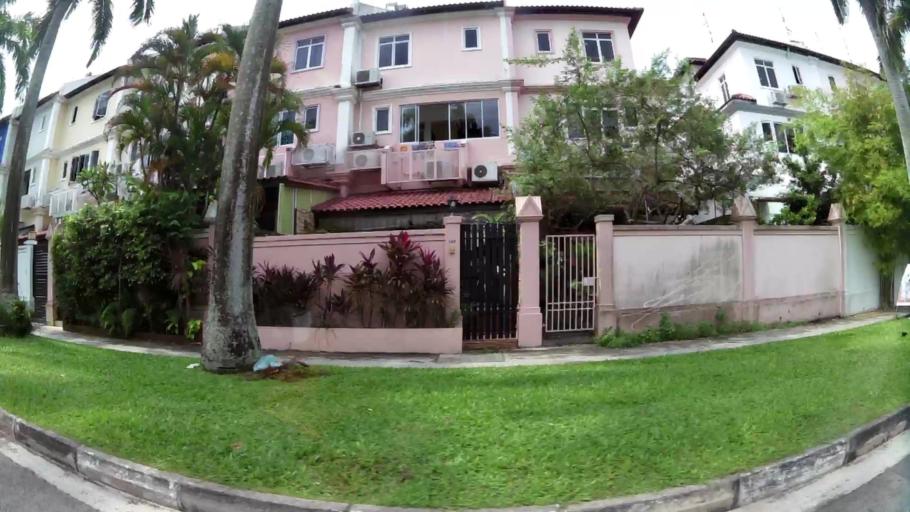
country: SG
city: Singapore
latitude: 1.3644
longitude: 103.9679
